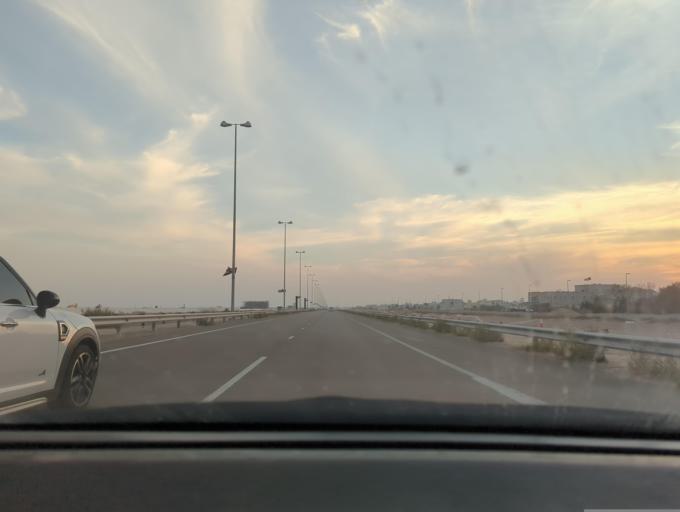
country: AE
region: Abu Dhabi
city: Abu Dhabi
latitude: 24.3551
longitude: 54.6639
